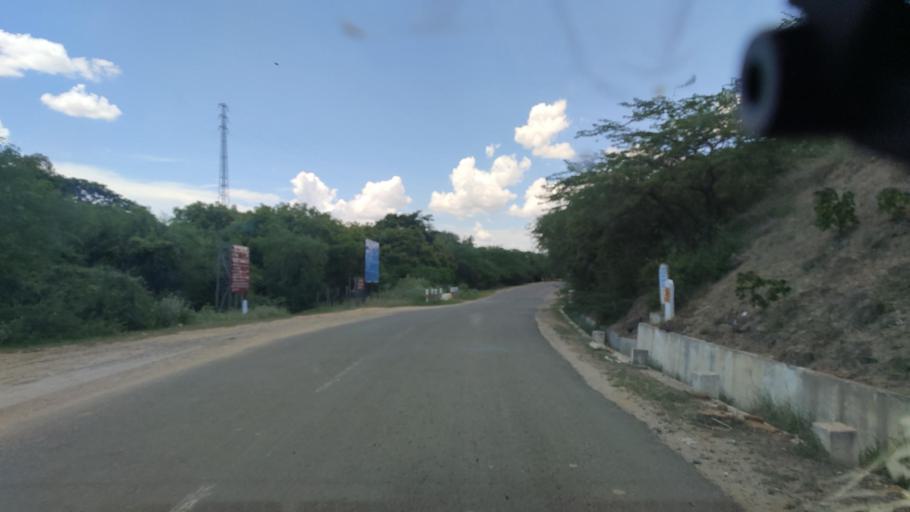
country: MM
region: Magway
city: Chauk
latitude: 20.9277
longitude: 94.8337
